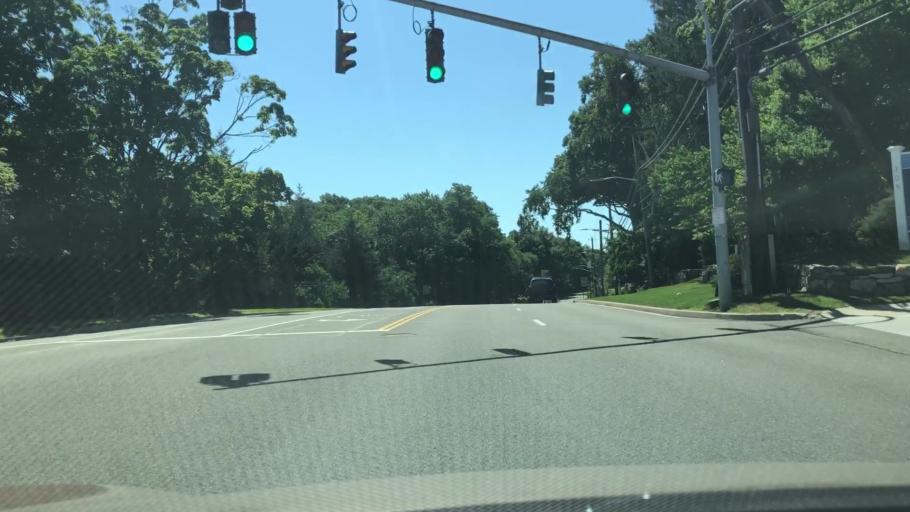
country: US
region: New York
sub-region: Westchester County
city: White Plains
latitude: 41.0270
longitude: -73.7463
